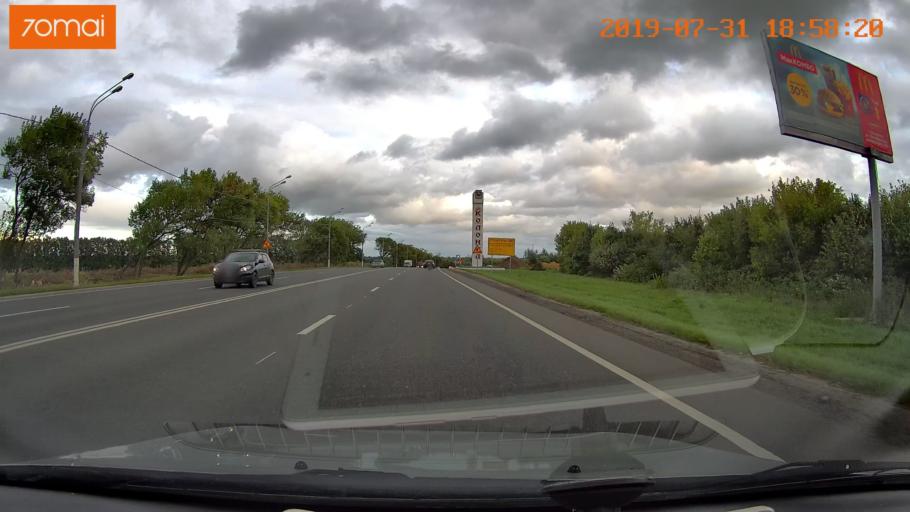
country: RU
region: Moskovskaya
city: Raduzhnyy
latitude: 55.1475
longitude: 38.7033
